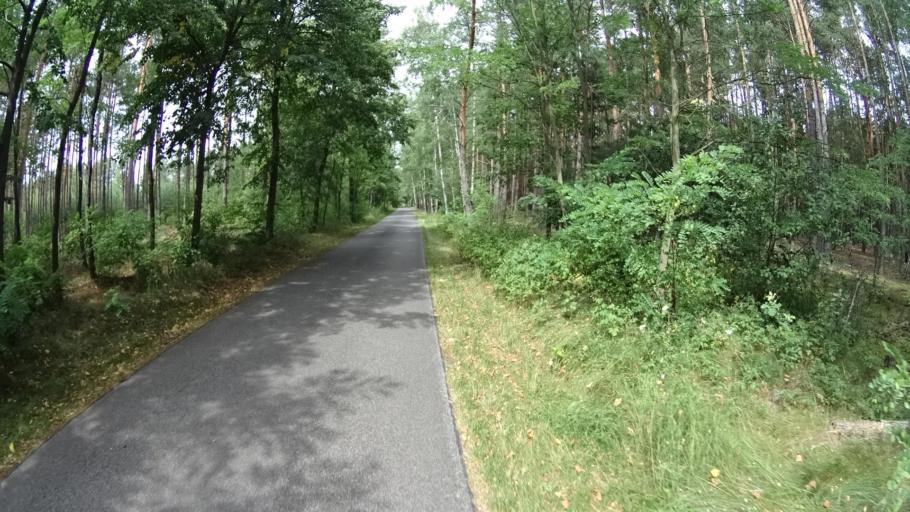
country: PL
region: Masovian Voivodeship
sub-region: Powiat bialobrzeski
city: Bialobrzegi
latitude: 51.6395
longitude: 20.9023
